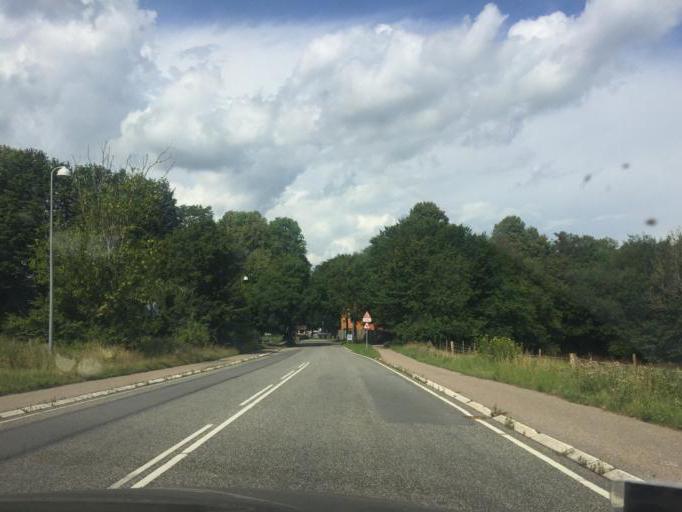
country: DK
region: Capital Region
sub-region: Rudersdal Kommune
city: Holte
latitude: 55.7795
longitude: 12.4472
